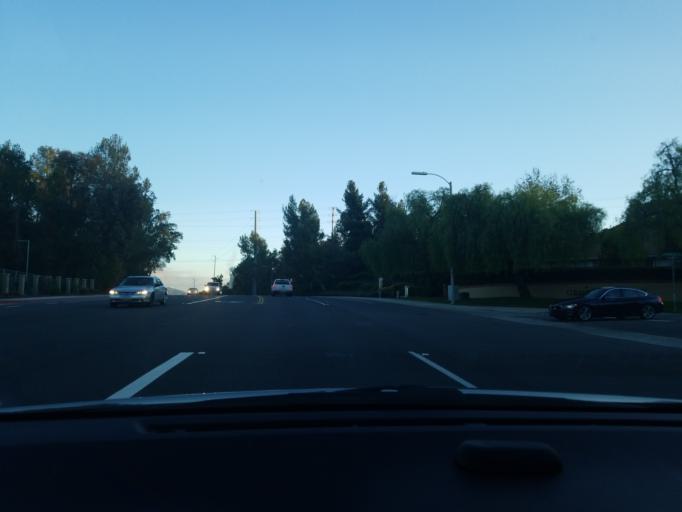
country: US
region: California
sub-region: Riverside County
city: Temecula
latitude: 33.5055
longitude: -117.1241
